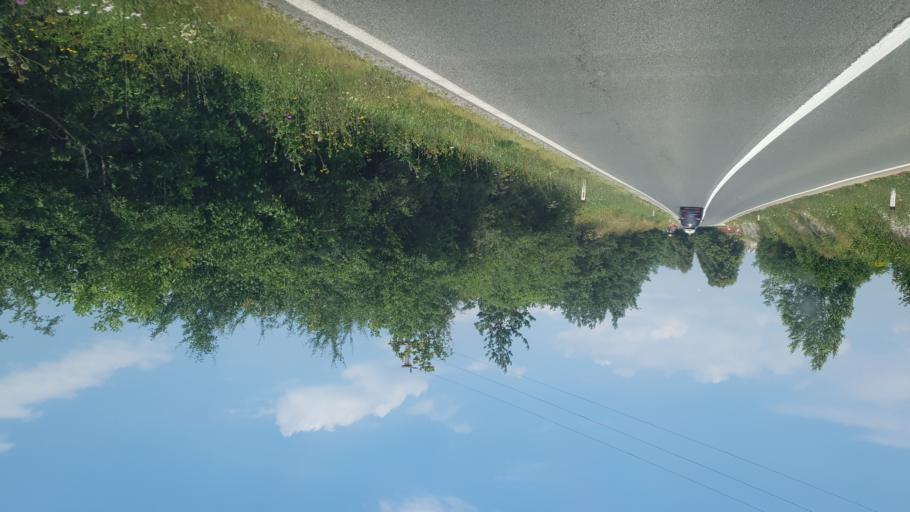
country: SI
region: Pivka
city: Pivka
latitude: 45.7230
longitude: 14.1911
